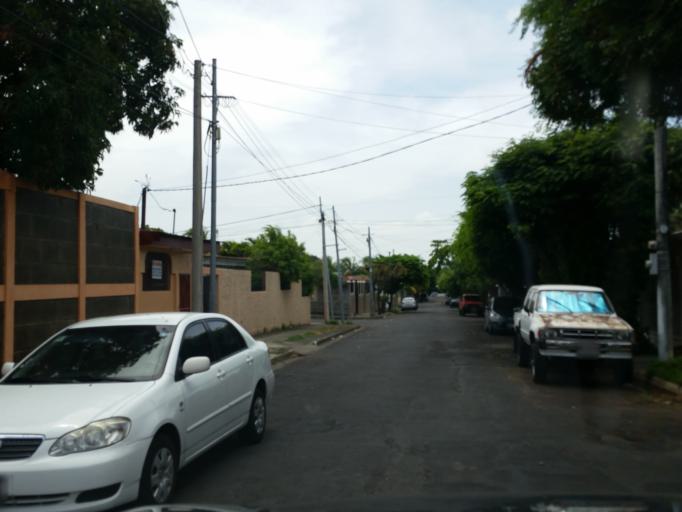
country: NI
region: Managua
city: Managua
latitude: 12.1239
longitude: -86.2509
